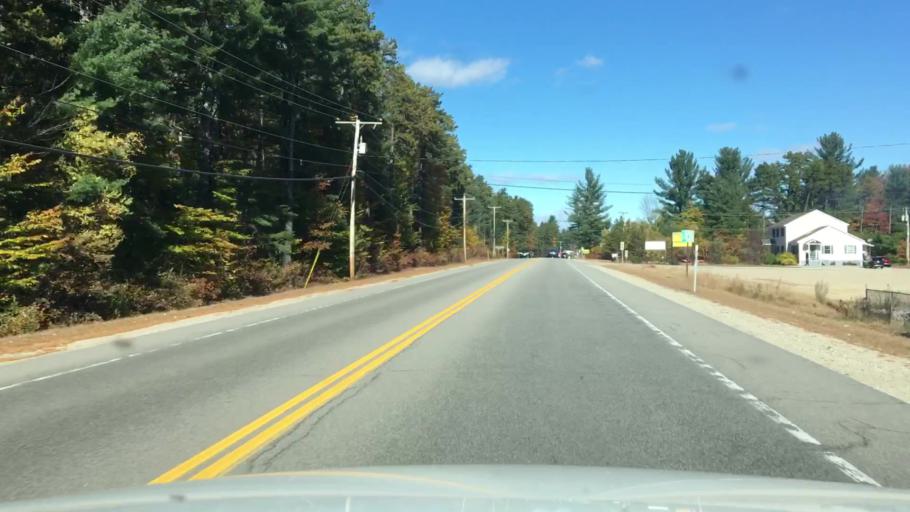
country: US
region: New Hampshire
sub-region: Carroll County
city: Tamworth
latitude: 43.8317
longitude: -71.2080
